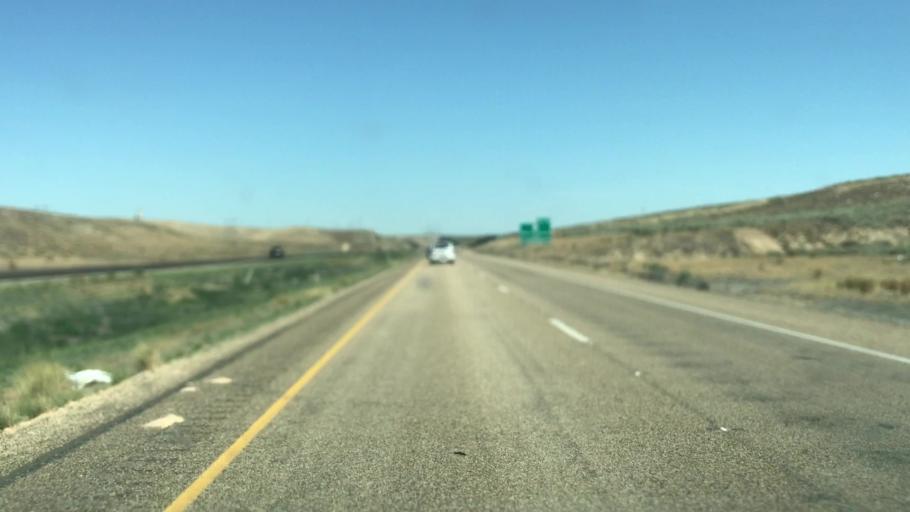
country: US
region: Idaho
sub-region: Payette County
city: New Plymouth
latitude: 43.8888
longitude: -116.8034
